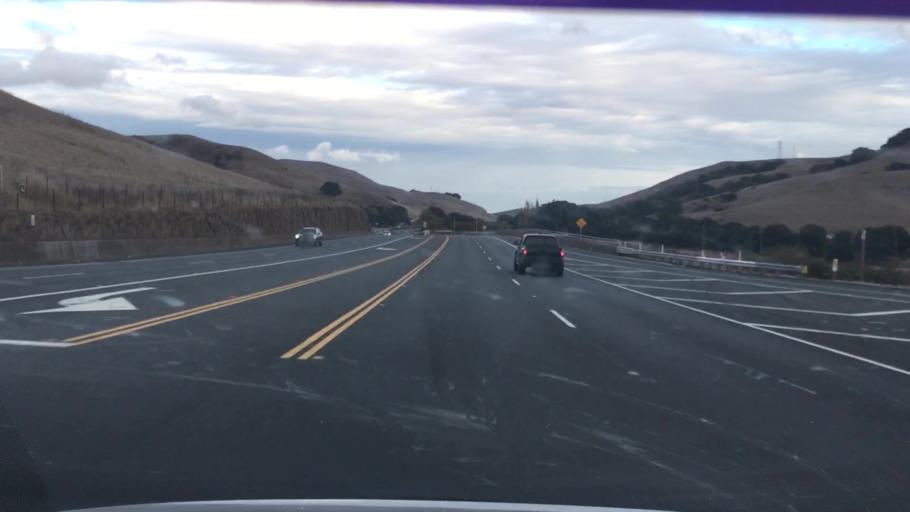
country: US
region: California
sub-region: Solano County
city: Green Valley
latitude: 38.2087
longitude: -122.1924
